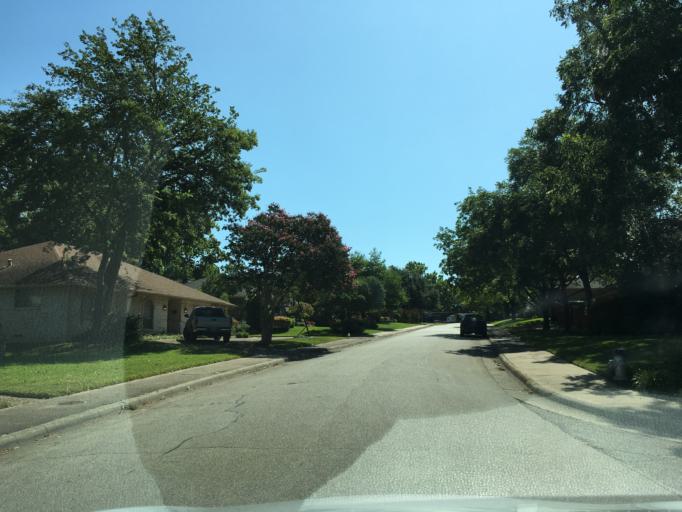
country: US
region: Texas
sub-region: Dallas County
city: Garland
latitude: 32.8686
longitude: -96.6962
